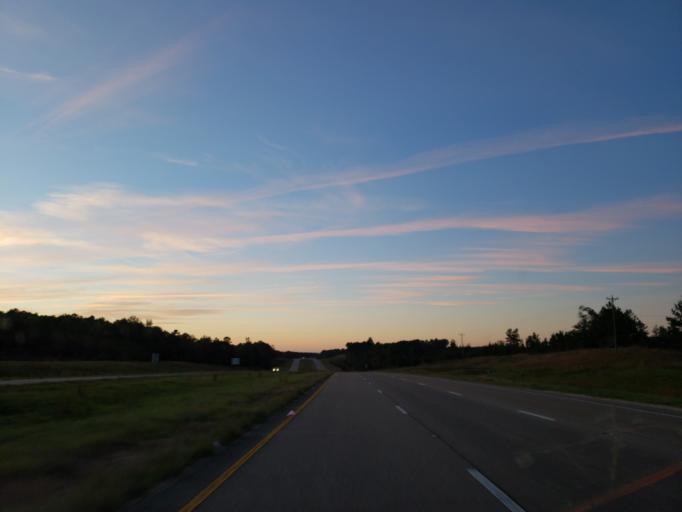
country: US
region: Mississippi
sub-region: Wayne County
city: Waynesboro
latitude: 31.7121
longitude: -88.6299
